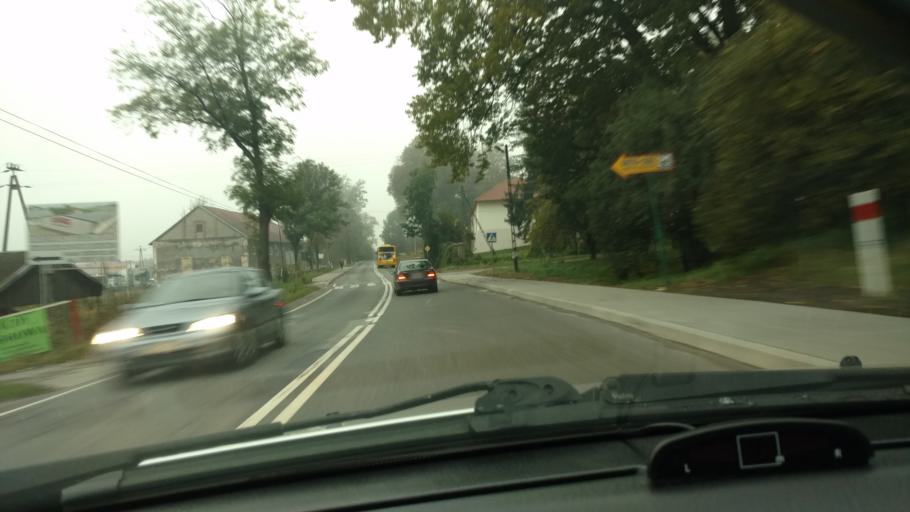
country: PL
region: Subcarpathian Voivodeship
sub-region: Powiat strzyzowski
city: Wisniowa
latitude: 49.8675
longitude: 21.6479
